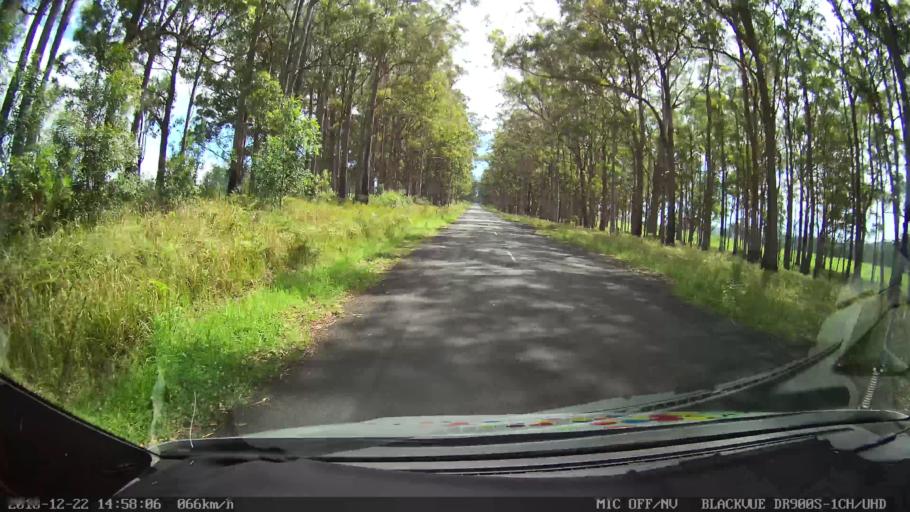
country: AU
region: New South Wales
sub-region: Bellingen
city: Dorrigo
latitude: -30.2382
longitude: 152.4943
